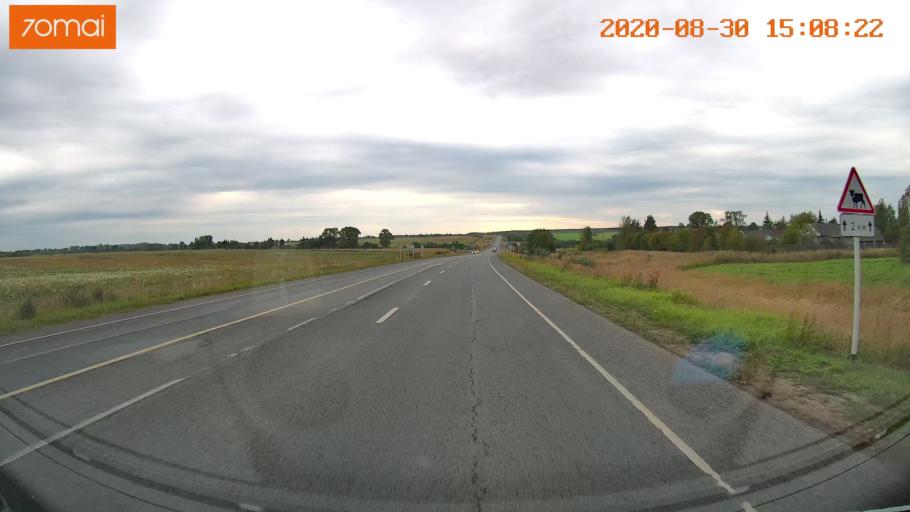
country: RU
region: Ivanovo
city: Staraya Vichuga
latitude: 57.2405
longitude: 41.8874
